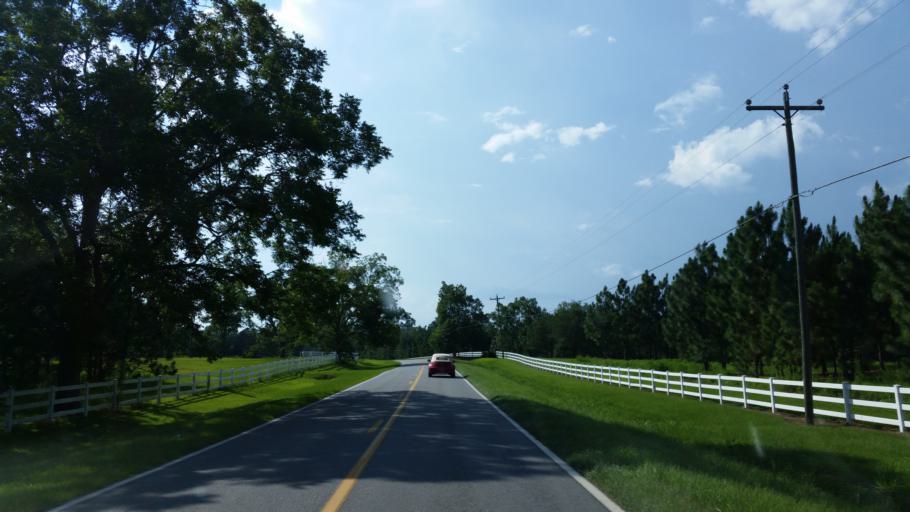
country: US
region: Georgia
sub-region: Lowndes County
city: Hahira
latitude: 30.9226
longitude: -83.3921
